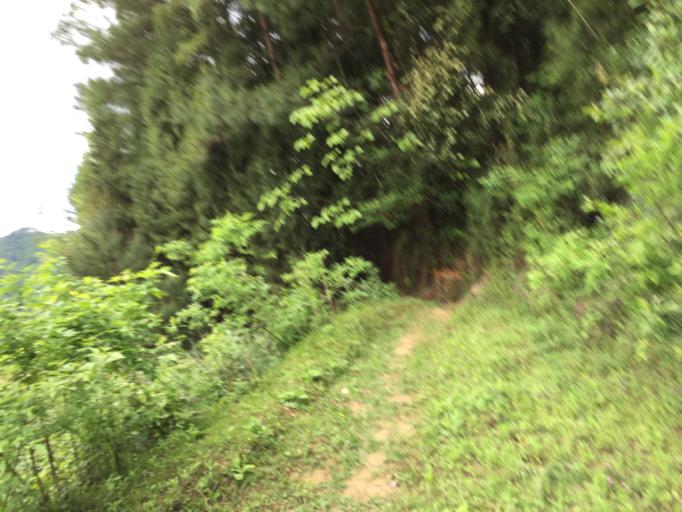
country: CN
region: Guizhou Sheng
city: Xujiaba
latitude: 27.6779
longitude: 108.0872
